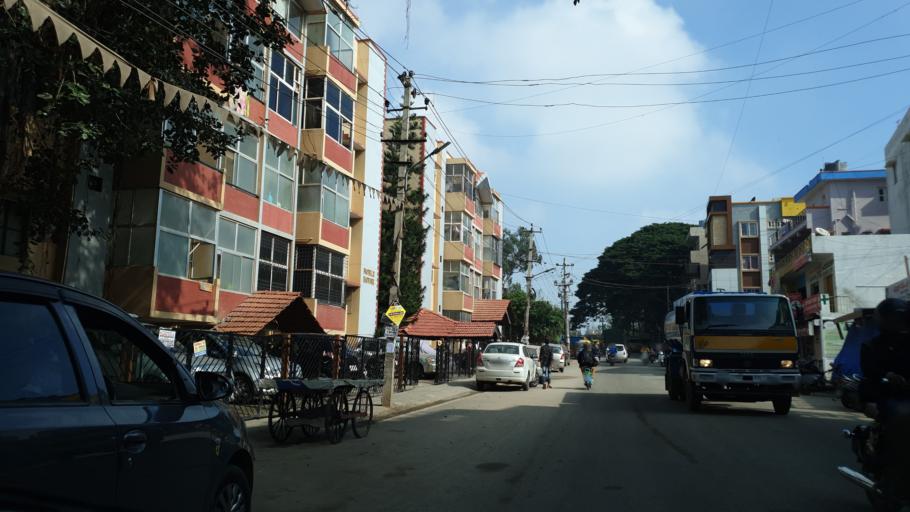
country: IN
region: Karnataka
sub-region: Bangalore Urban
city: Bangalore
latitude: 12.9683
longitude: 77.6826
